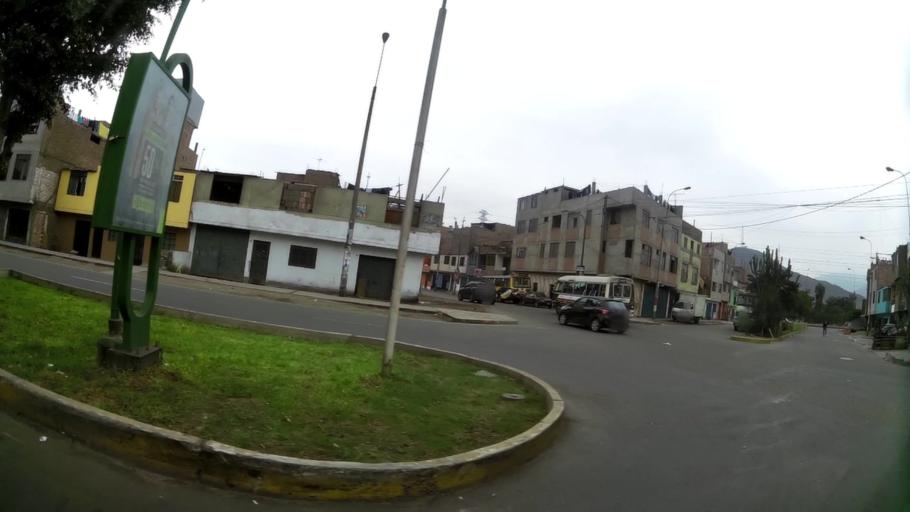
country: PE
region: Lima
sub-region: Lima
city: San Luis
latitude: -12.0409
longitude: -76.9773
